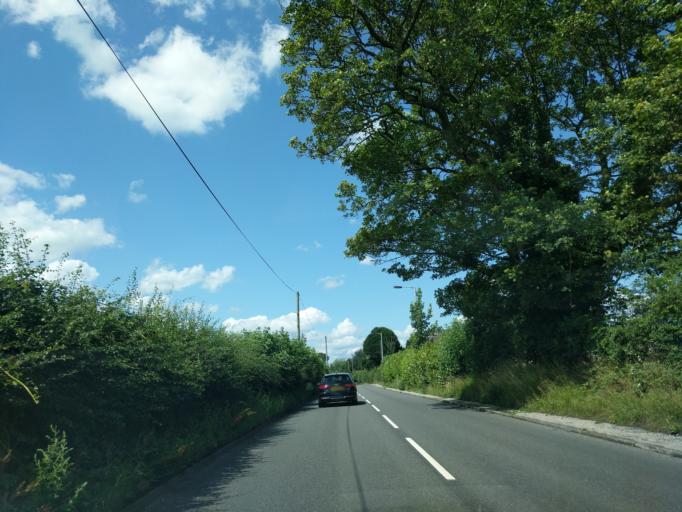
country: GB
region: England
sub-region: Staffordshire
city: Cheadle
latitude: 52.9484
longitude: -1.9816
